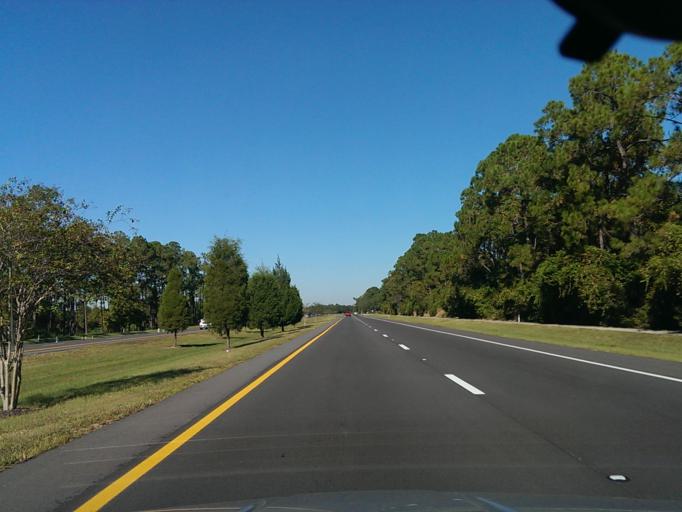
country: US
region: Florida
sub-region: Orange County
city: Bay Hill
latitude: 28.4390
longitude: -81.5387
